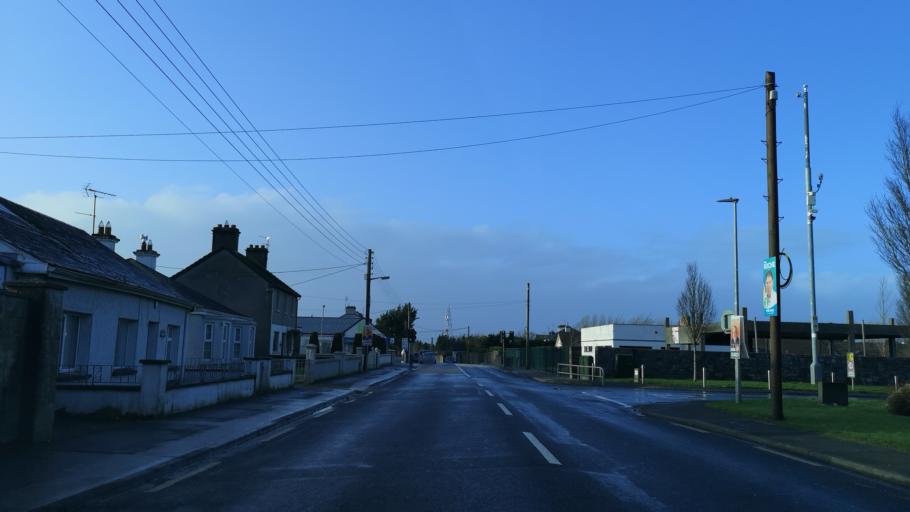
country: IE
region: Connaught
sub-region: County Galway
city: Tuam
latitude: 53.5098
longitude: -8.8428
